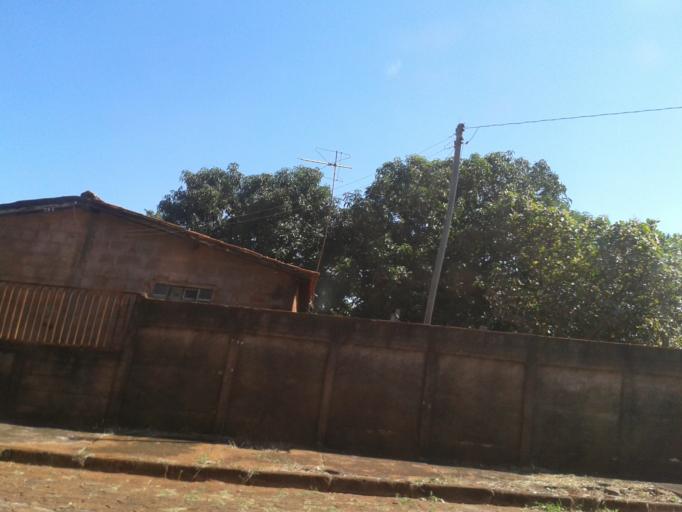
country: BR
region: Minas Gerais
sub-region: Centralina
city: Centralina
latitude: -18.7235
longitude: -49.2059
